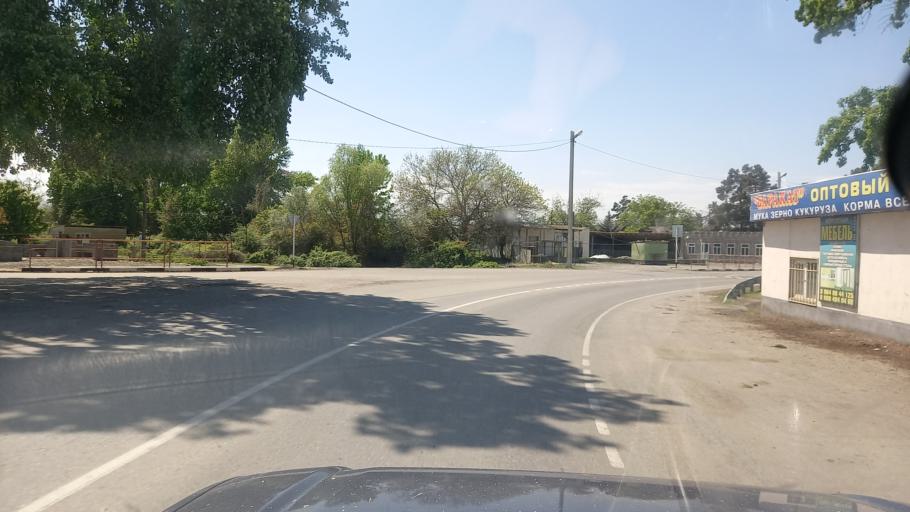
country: AZ
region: Qusar
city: Samur
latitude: 41.7257
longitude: 48.4581
